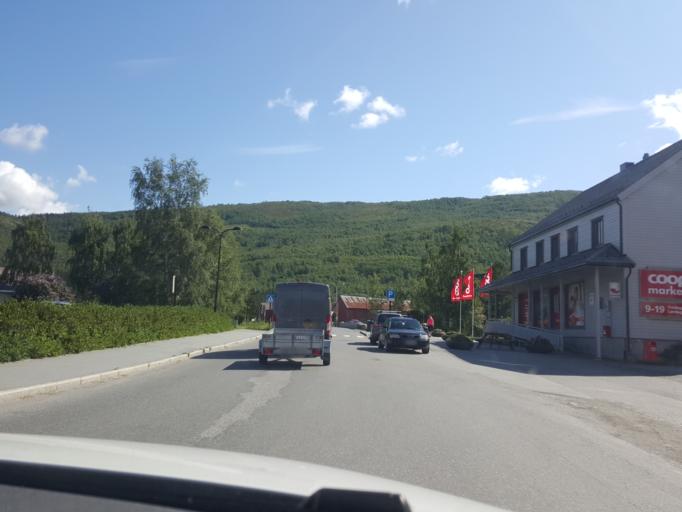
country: NO
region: Nordland
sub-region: Bodo
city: Loding
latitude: 67.1163
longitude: 15.0054
